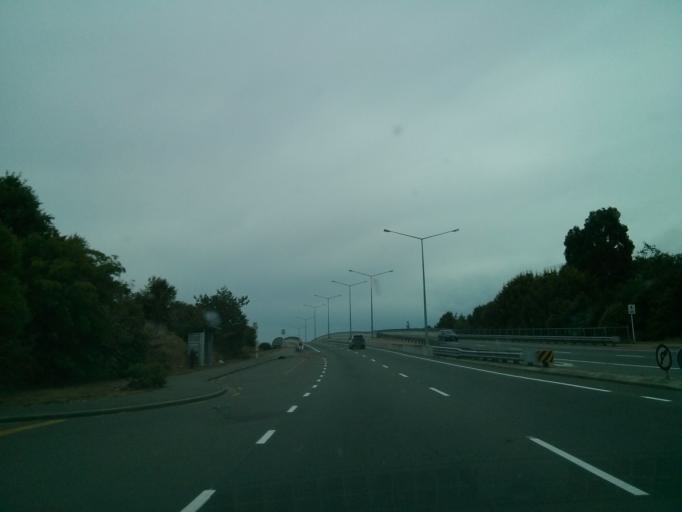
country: NZ
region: Canterbury
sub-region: Christchurch City
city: Christchurch
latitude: -43.4678
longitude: 172.6178
